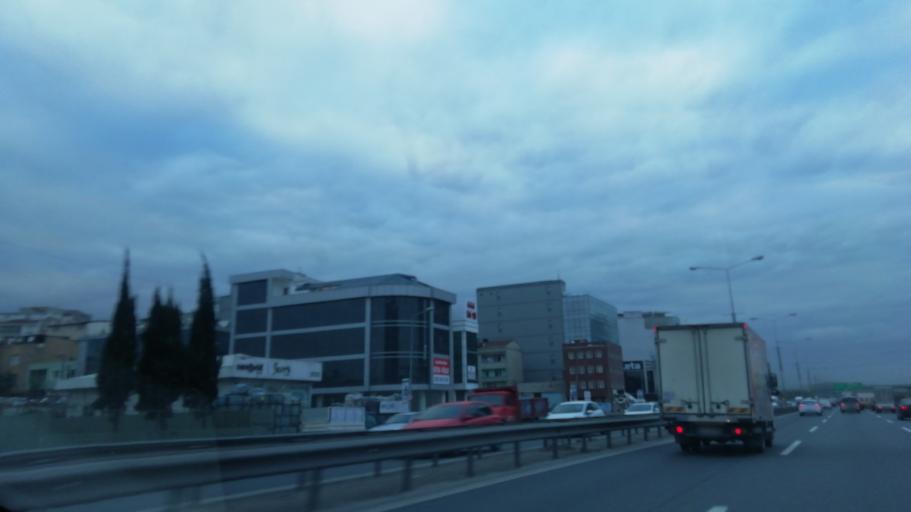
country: TR
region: Istanbul
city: Mahmutbey
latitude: 41.0517
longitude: 28.8090
